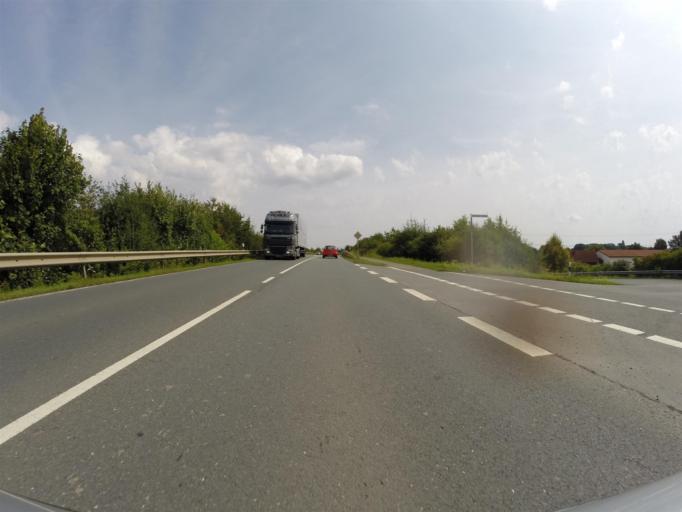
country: DE
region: North Rhine-Westphalia
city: Loehne
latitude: 52.1857
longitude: 8.6626
